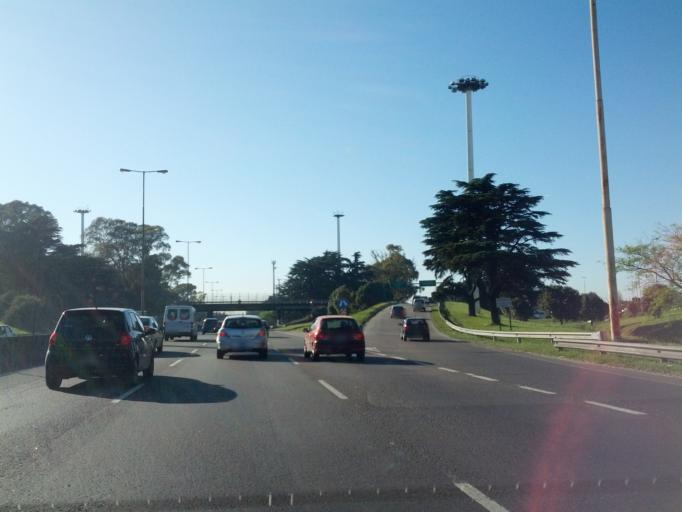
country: AR
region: Buenos Aires F.D.
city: Villa Lugano
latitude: -34.6847
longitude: -58.4883
